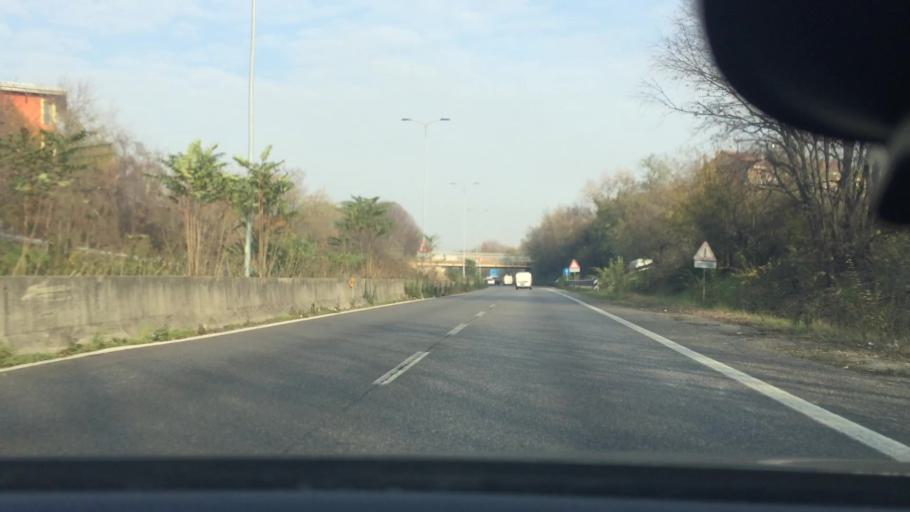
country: IT
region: Lombardy
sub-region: Citta metropolitana di Milano
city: Cormano
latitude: 45.5474
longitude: 9.1631
